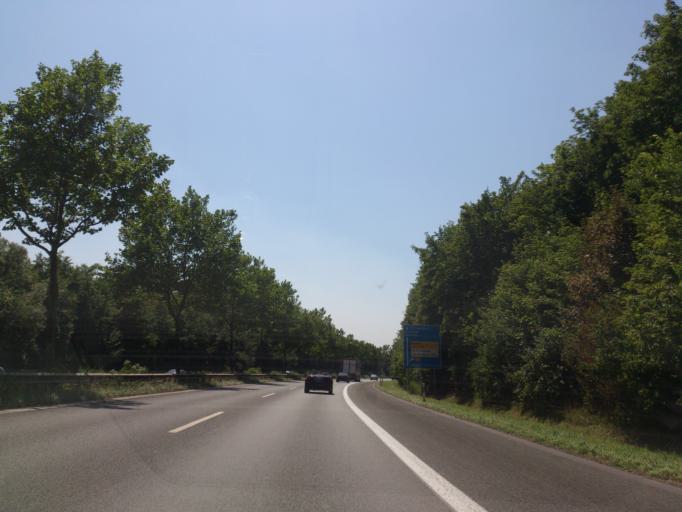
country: DE
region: North Rhine-Westphalia
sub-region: Regierungsbezirk Detmold
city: Bielefeld
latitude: 51.9869
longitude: 8.4947
